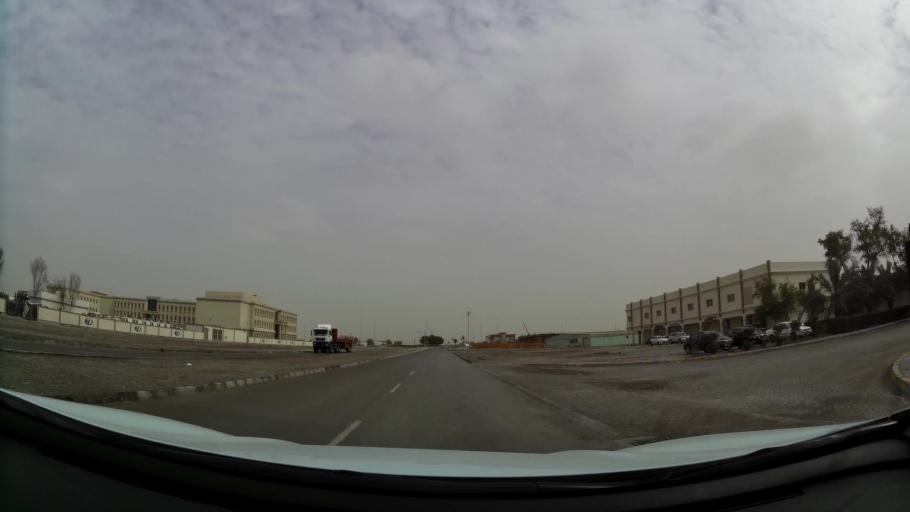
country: AE
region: Abu Dhabi
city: Abu Dhabi
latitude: 24.3535
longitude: 54.4698
